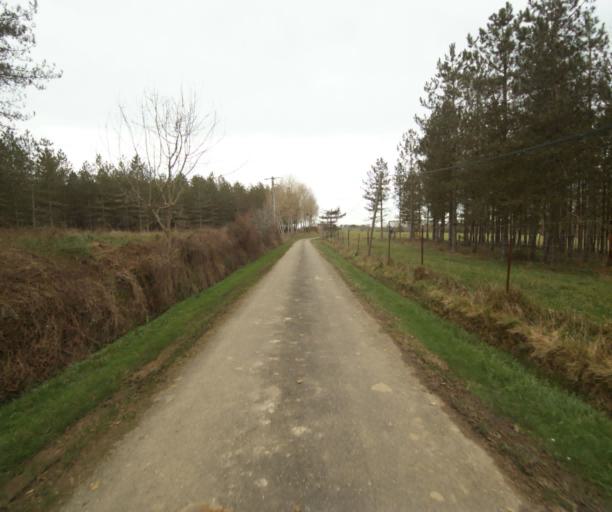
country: FR
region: Aquitaine
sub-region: Departement des Landes
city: Gabarret
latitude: 43.9353
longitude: 0.0279
